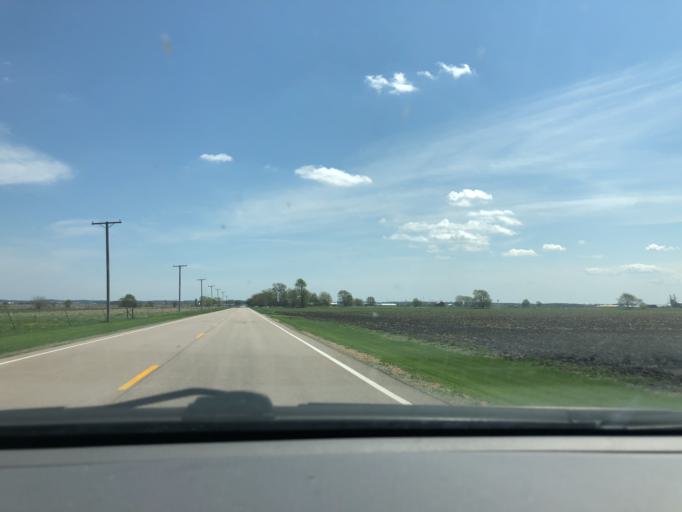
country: US
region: Illinois
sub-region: Kane County
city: Hampshire
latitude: 42.1100
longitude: -88.5820
